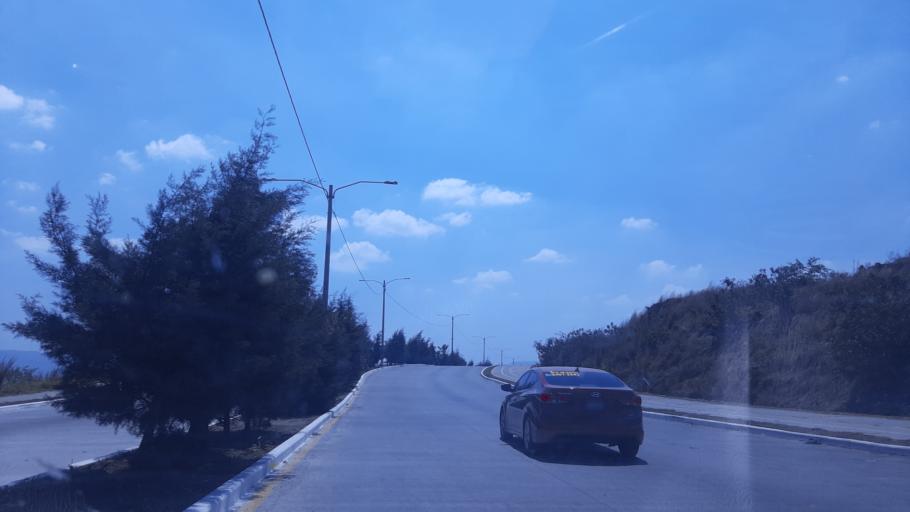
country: GT
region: Guatemala
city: Villa Nueva
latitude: 14.5155
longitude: -90.5909
